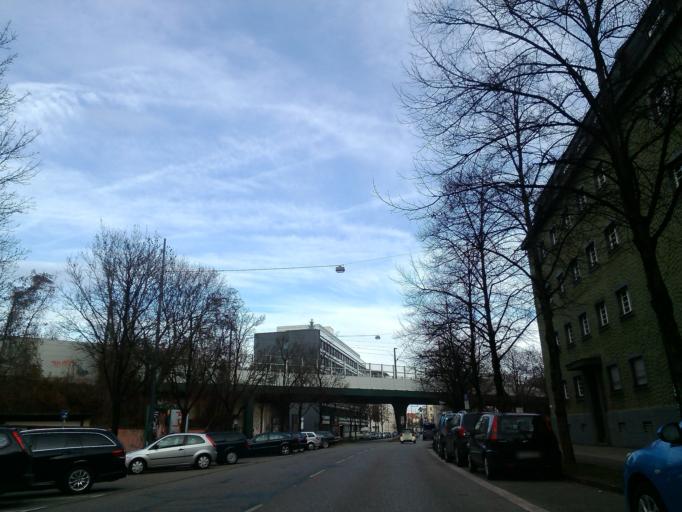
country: DE
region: Bavaria
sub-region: Upper Bavaria
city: Munich
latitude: 48.1168
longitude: 11.5734
